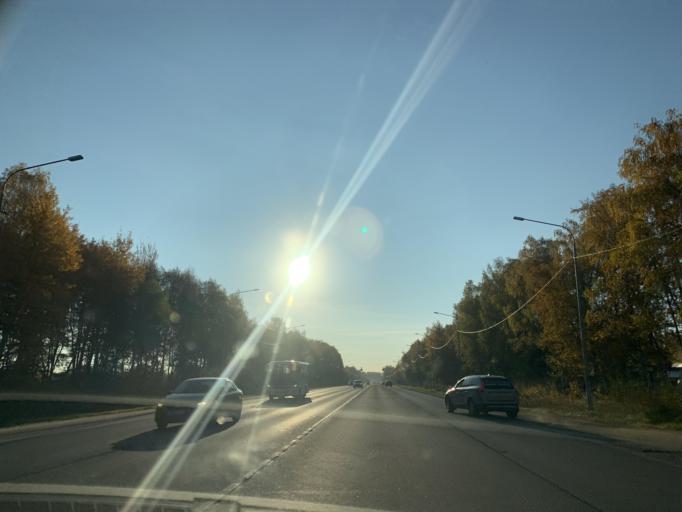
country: RU
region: Jaroslavl
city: Konstantinovskiy
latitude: 57.7466
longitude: 39.7124
